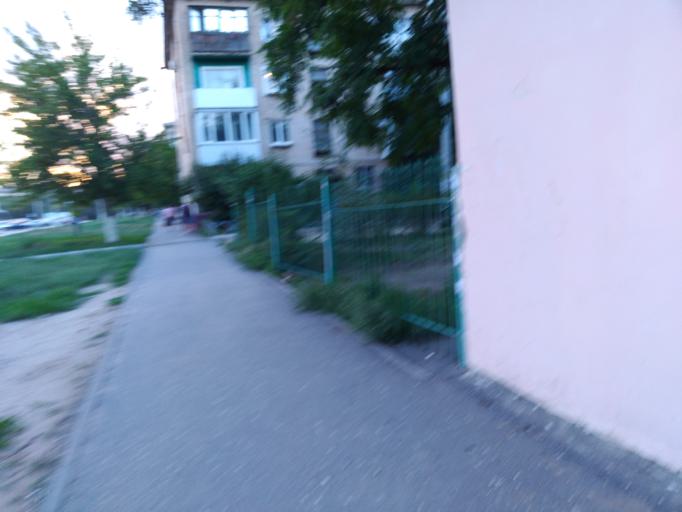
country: RU
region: Volgograd
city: Volgograd
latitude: 48.6733
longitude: 44.4463
